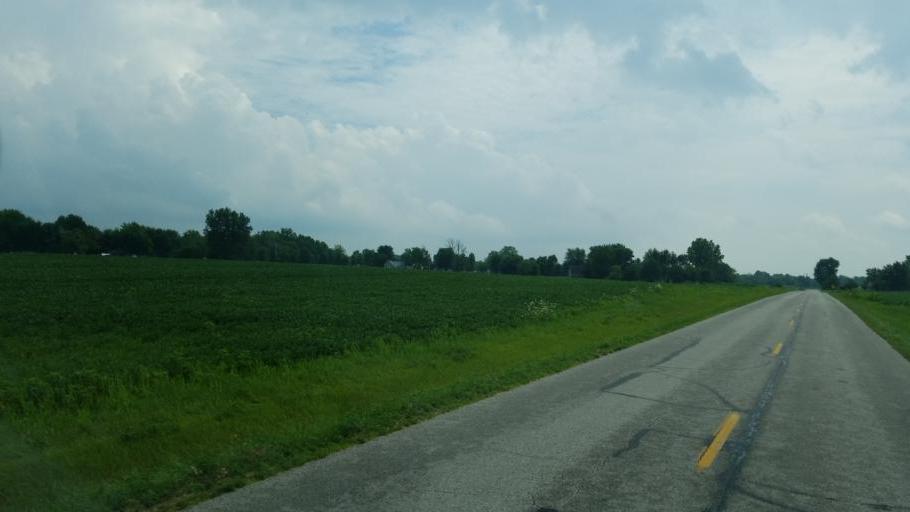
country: US
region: Ohio
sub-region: Union County
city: Marysville
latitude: 40.3439
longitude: -83.4208
